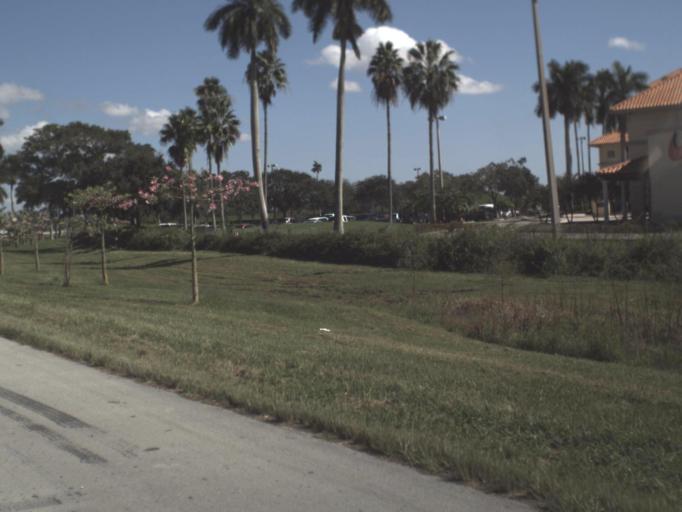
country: US
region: Florida
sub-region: Miami-Dade County
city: Florida City
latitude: 25.4533
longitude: -80.4745
